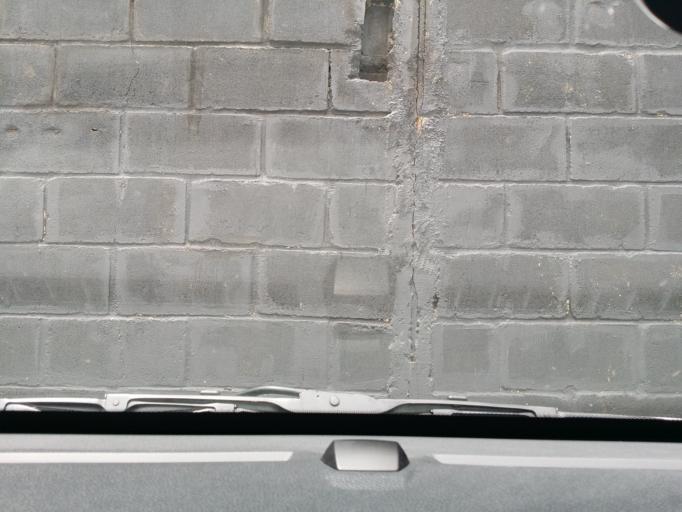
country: BR
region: Sao Paulo
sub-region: Sao Carlos
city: Sao Carlos
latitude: -22.0240
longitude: -47.8941
